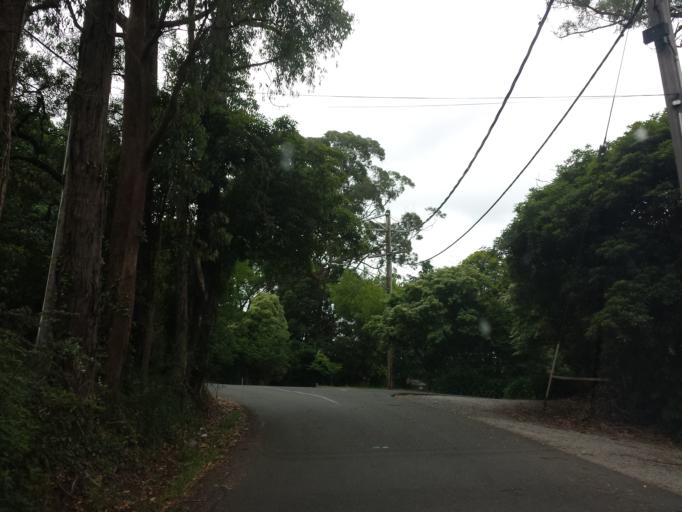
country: AU
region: Victoria
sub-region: Yarra Ranges
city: Belgrave Heights
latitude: -37.9162
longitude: 145.3361
